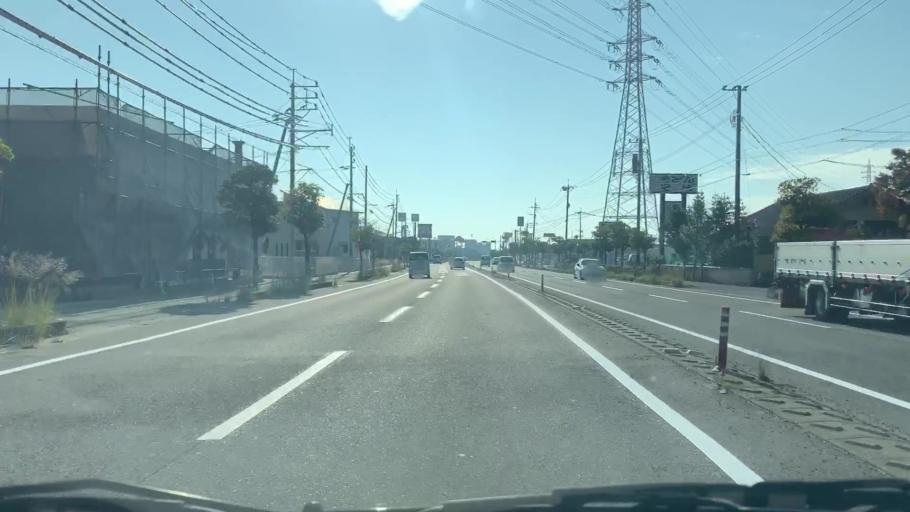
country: JP
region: Saga Prefecture
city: Saga-shi
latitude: 33.2960
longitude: 130.2826
